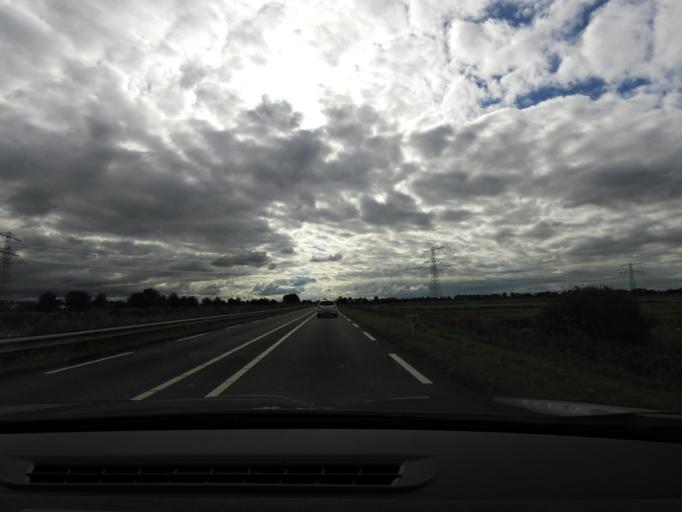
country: NL
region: South Holland
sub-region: Gemeente Brielle
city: Brielle
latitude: 51.8609
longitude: 4.2104
